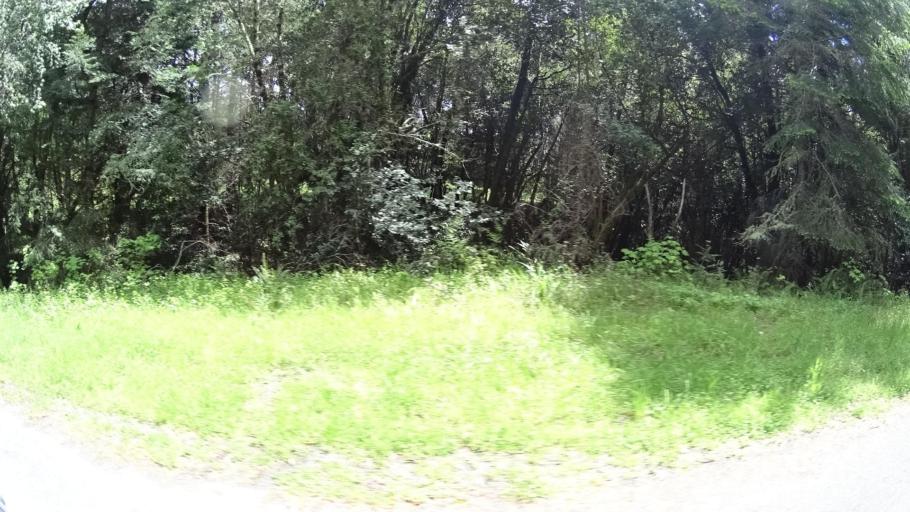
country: US
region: California
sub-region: Humboldt County
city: Blue Lake
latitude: 40.8447
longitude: -123.9148
